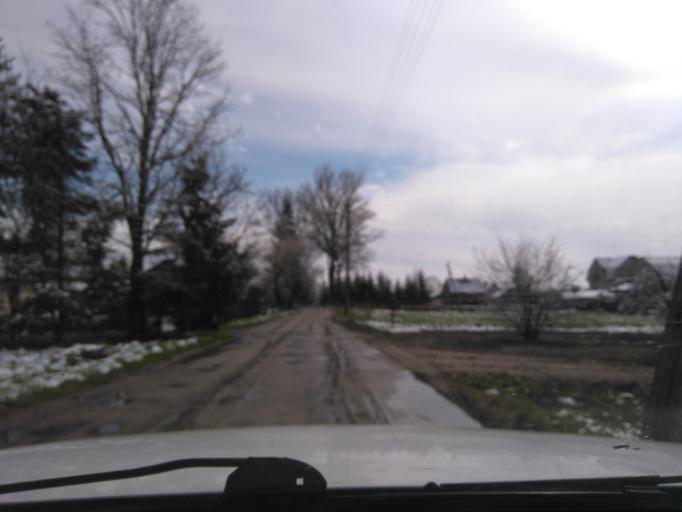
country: LT
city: Virbalis
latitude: 54.6301
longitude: 22.8250
